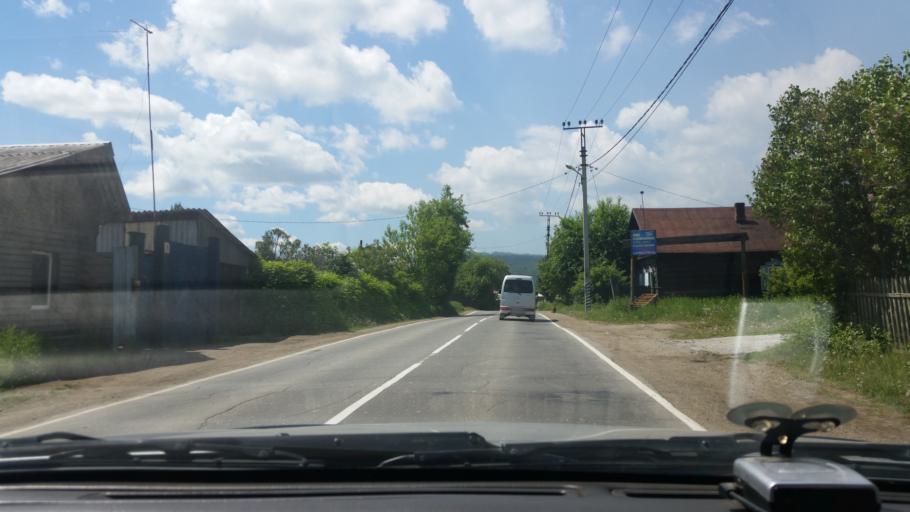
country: RU
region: Irkutsk
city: Shelekhov
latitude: 52.1554
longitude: 104.0808
